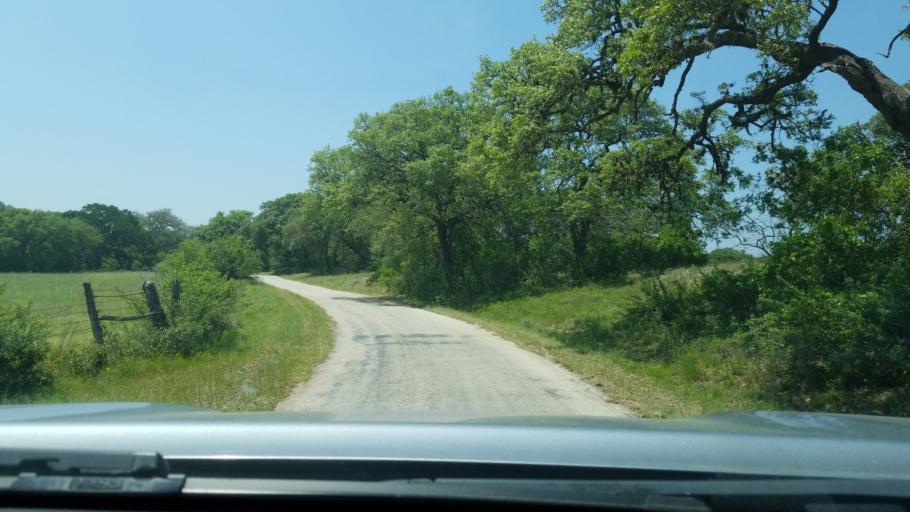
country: US
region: Texas
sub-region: Blanco County
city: Blanco
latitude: 30.0151
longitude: -98.4479
